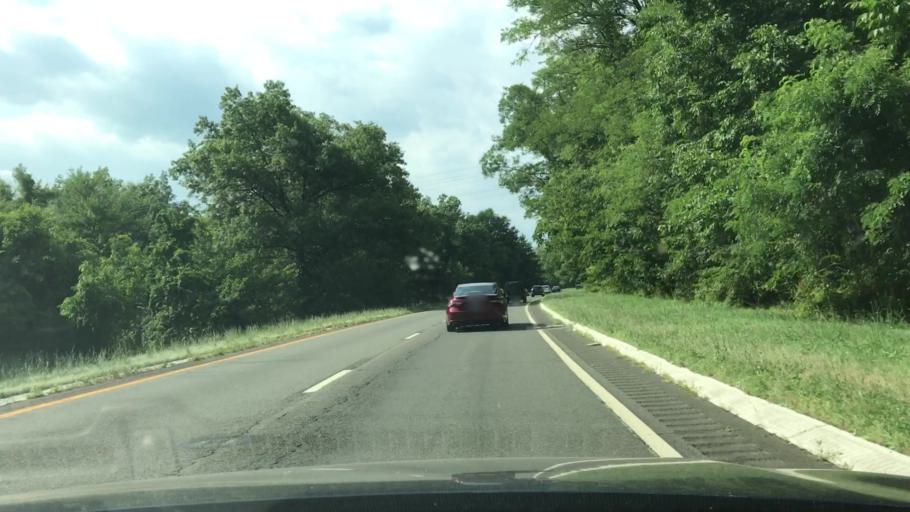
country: US
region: New York
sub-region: Rockland County
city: Bardonia
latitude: 41.1113
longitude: -74.0009
